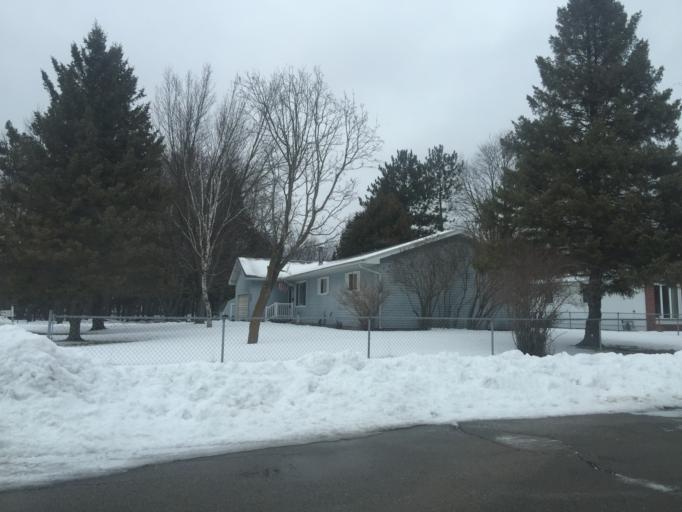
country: US
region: Michigan
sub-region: Menominee County
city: Menominee
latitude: 45.1384
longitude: -87.6187
